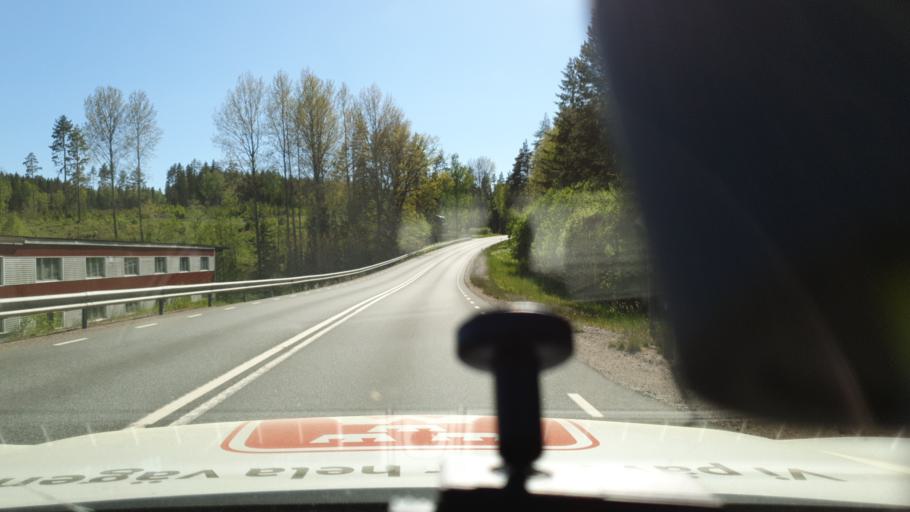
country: SE
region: Kalmar
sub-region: Hultsfreds Kommun
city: Virserum
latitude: 57.3967
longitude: 15.4904
